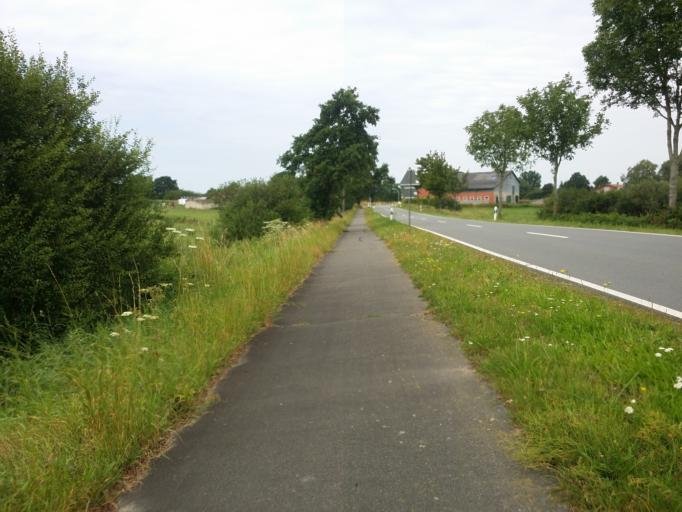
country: DE
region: Schleswig-Holstein
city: Huje
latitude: 53.9715
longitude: 9.4416
